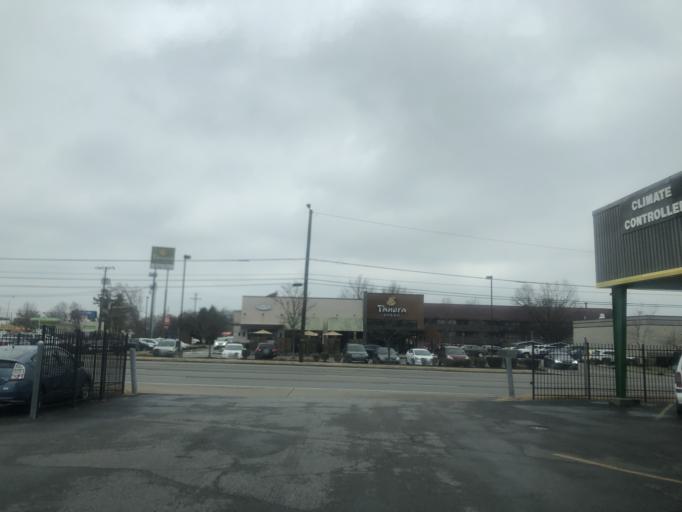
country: US
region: Tennessee
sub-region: Davidson County
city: Lakewood
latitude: 36.1465
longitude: -86.6681
